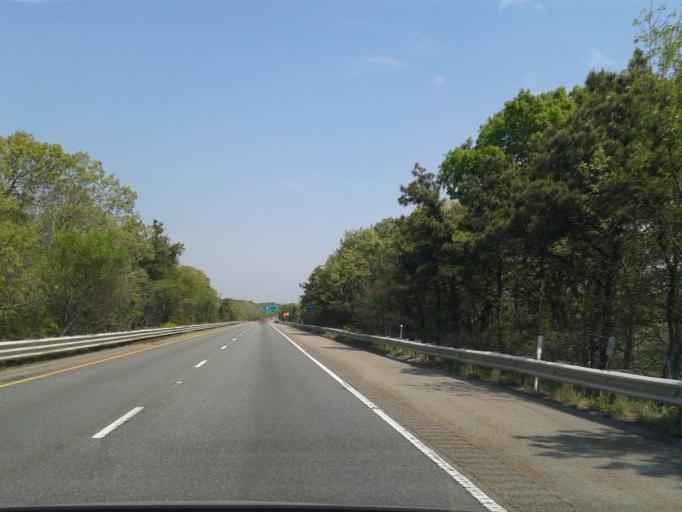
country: US
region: Massachusetts
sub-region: Barnstable County
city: Sagamore
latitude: 41.8118
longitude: -70.5524
